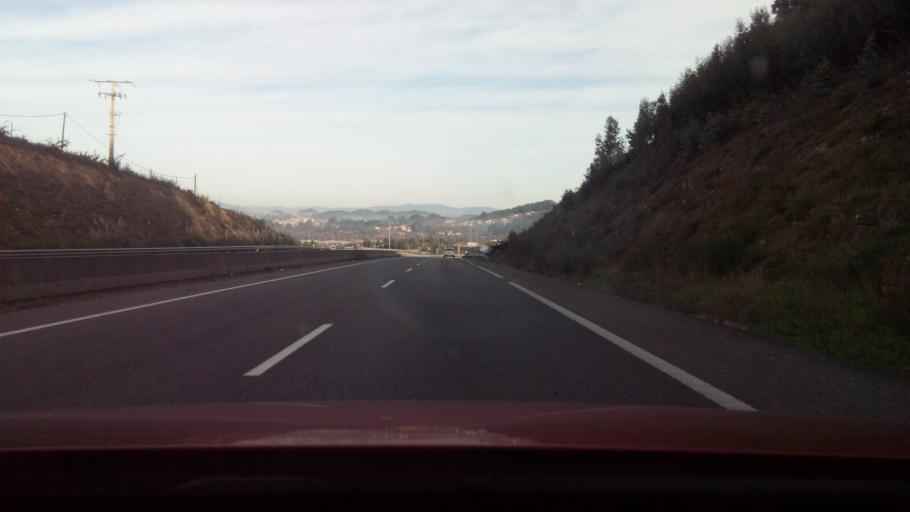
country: ES
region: Galicia
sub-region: Provincia de Pontevedra
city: Sanxenxo
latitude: 42.4225
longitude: -8.8072
